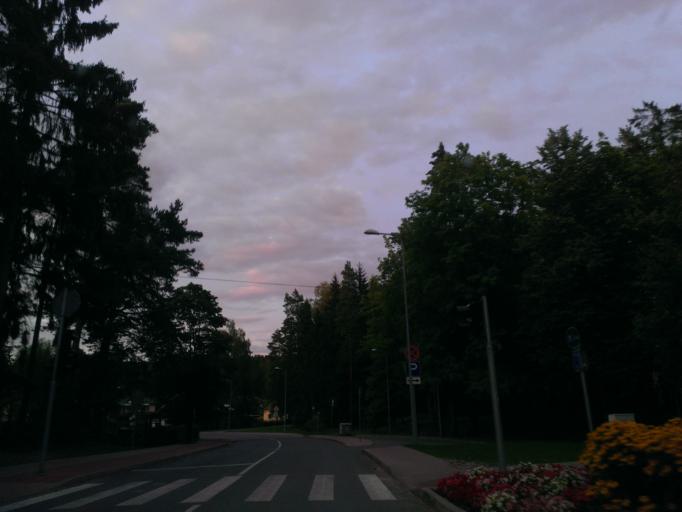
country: LV
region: Ogre
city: Ogre
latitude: 56.8201
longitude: 24.6112
